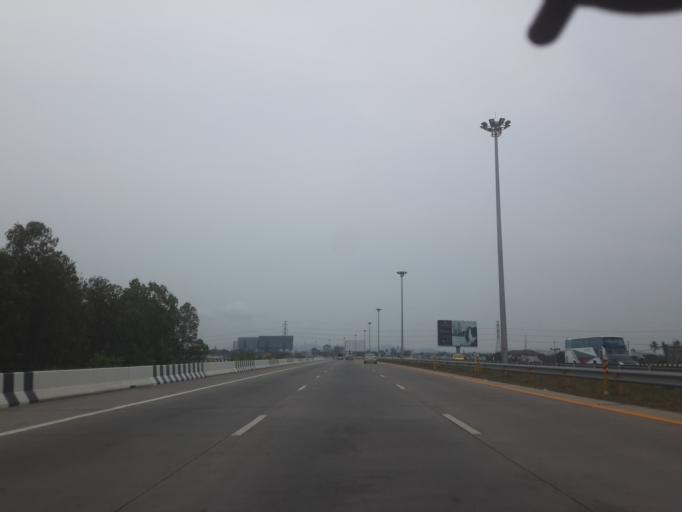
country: TH
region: Chon Buri
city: Phatthaya
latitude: 12.9439
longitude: 100.9207
